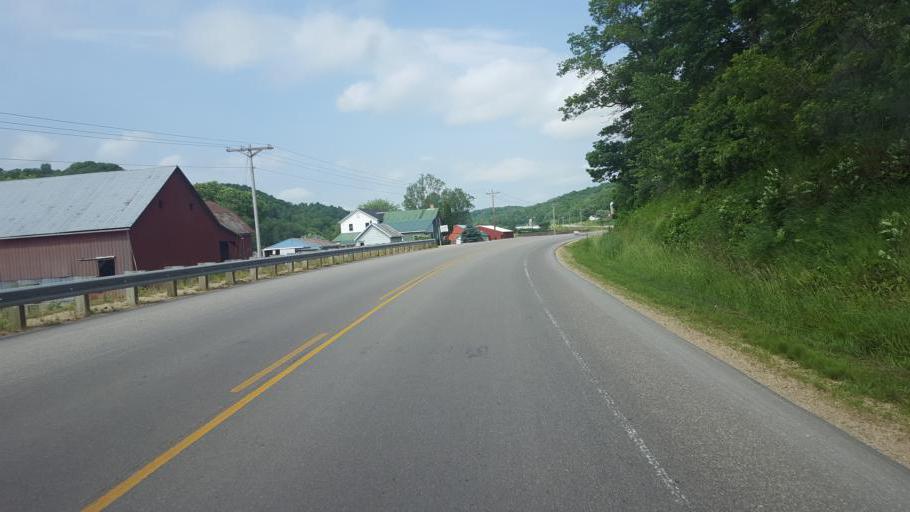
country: US
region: Wisconsin
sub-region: Monroe County
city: Cashton
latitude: 43.7324
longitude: -90.6839
